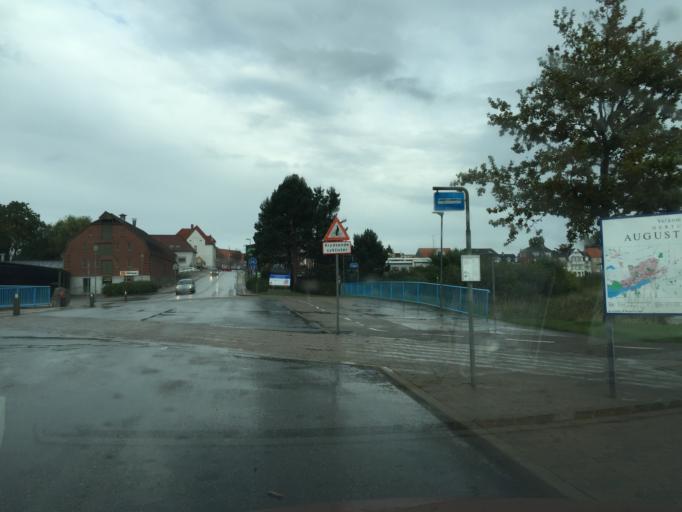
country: DK
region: South Denmark
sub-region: Sonderborg Kommune
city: Augustenborg
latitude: 54.9442
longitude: 9.8735
